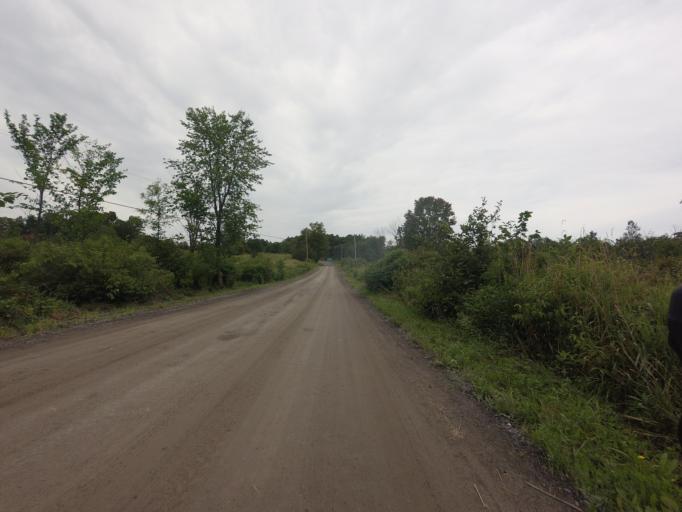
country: CA
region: Ontario
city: Kingston
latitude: 44.5547
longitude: -76.6207
